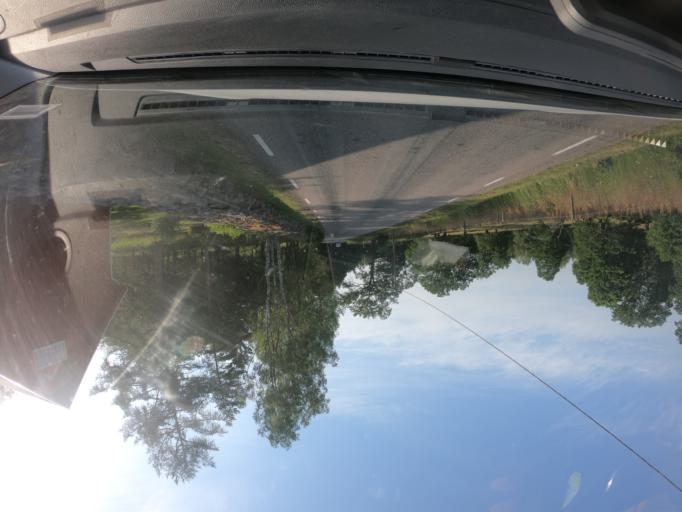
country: SE
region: Skane
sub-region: Orkelljunga Kommun
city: OErkelljunga
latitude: 56.2771
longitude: 13.3936
